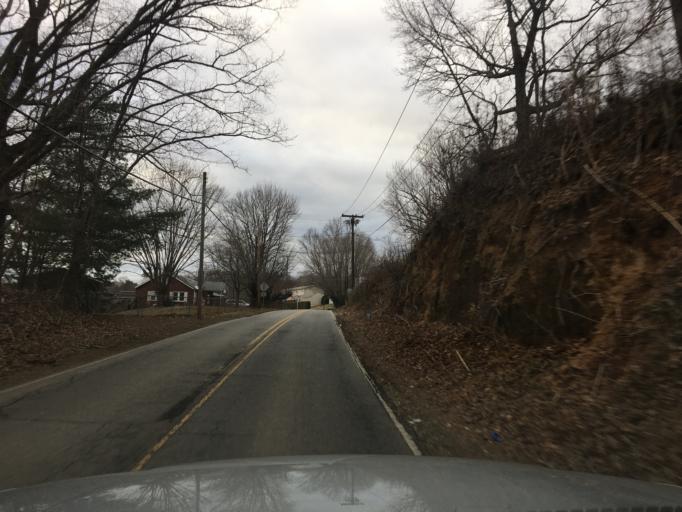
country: US
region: North Carolina
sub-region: Buncombe County
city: Asheville
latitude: 35.5973
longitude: -82.5790
